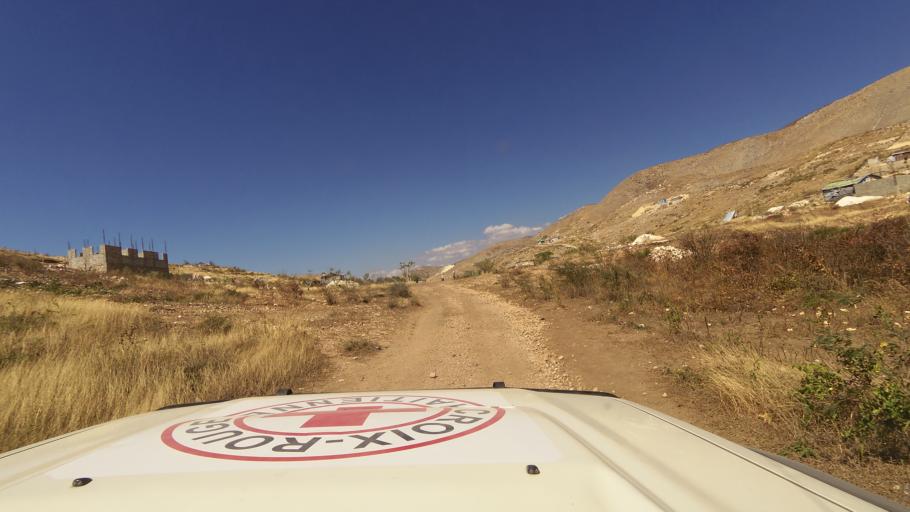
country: HT
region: Ouest
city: Croix des Bouquets
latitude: 18.6779
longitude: -72.2940
